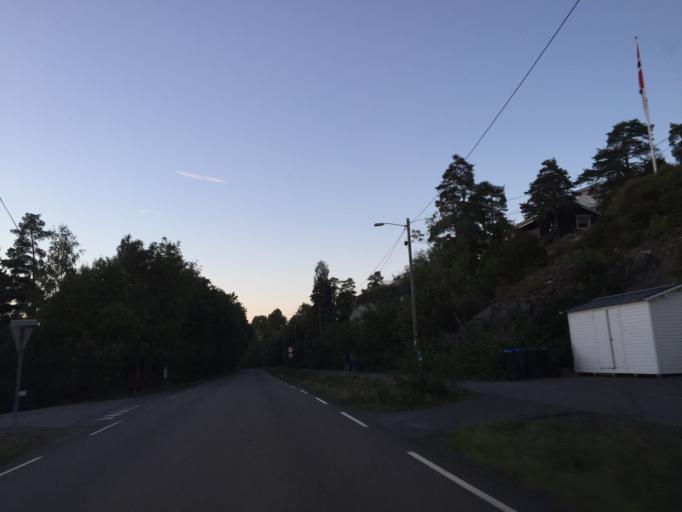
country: NO
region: Ostfold
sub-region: Moss
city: Moss
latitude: 59.5084
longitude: 10.6856
